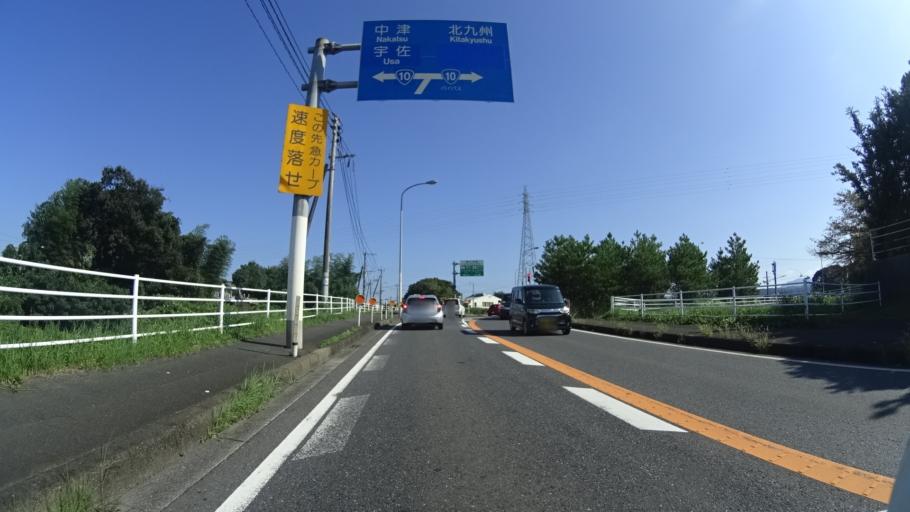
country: JP
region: Fukuoka
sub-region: Buzen-shi
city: Buzen
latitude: 33.6138
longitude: 131.1019
